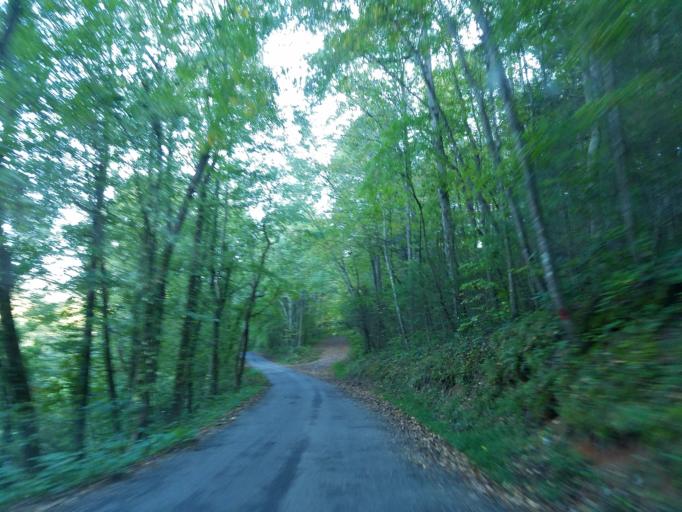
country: US
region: Georgia
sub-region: Pickens County
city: Jasper
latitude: 34.6272
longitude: -84.2539
